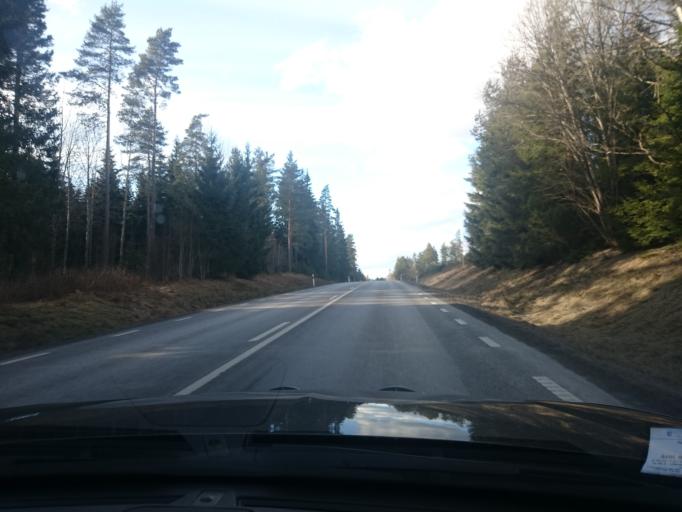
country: SE
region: Joenkoeping
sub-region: Vetlanda Kommun
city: Vetlanda
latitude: 57.3731
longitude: 15.0962
